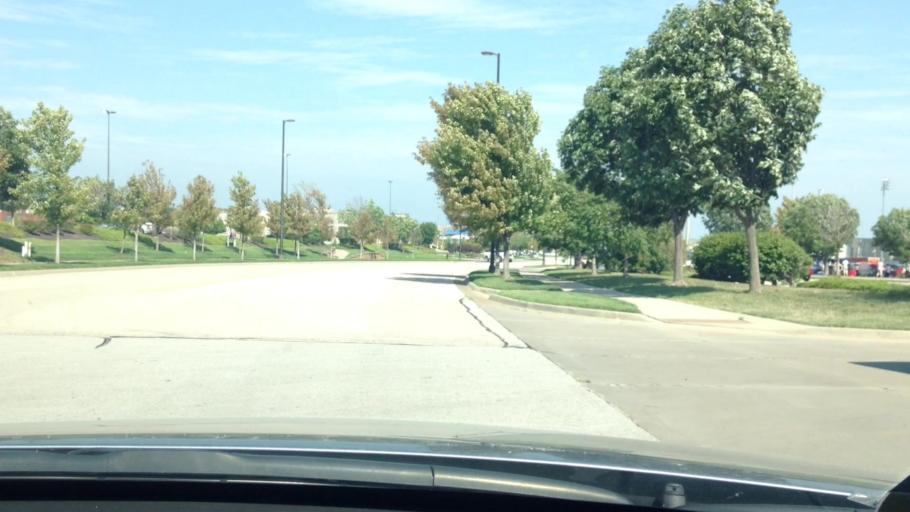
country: US
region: Kansas
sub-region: Wyandotte County
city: Edwardsville
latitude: 39.1255
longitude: -94.8341
